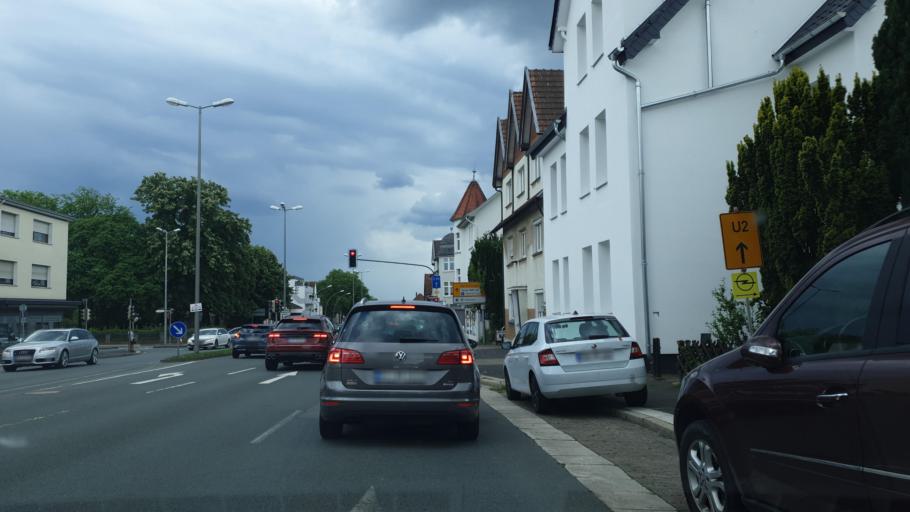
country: DE
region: North Rhine-Westphalia
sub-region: Regierungsbezirk Detmold
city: Herford
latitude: 52.1269
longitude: 8.6852
